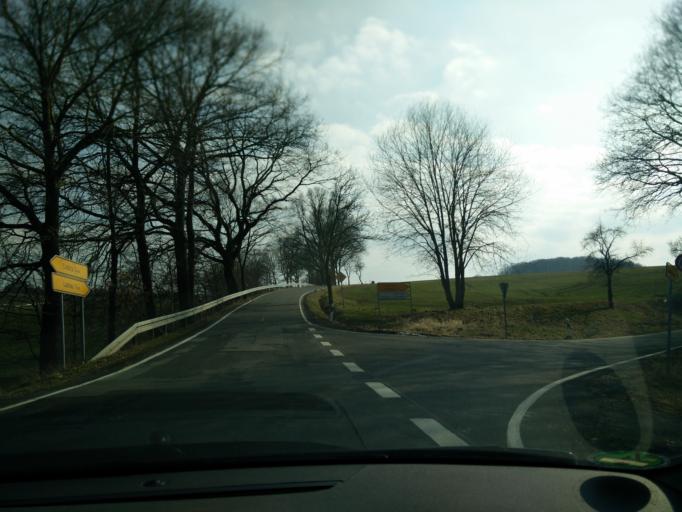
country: DE
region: Saxony
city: Colditz
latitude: 51.1111
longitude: 12.8167
